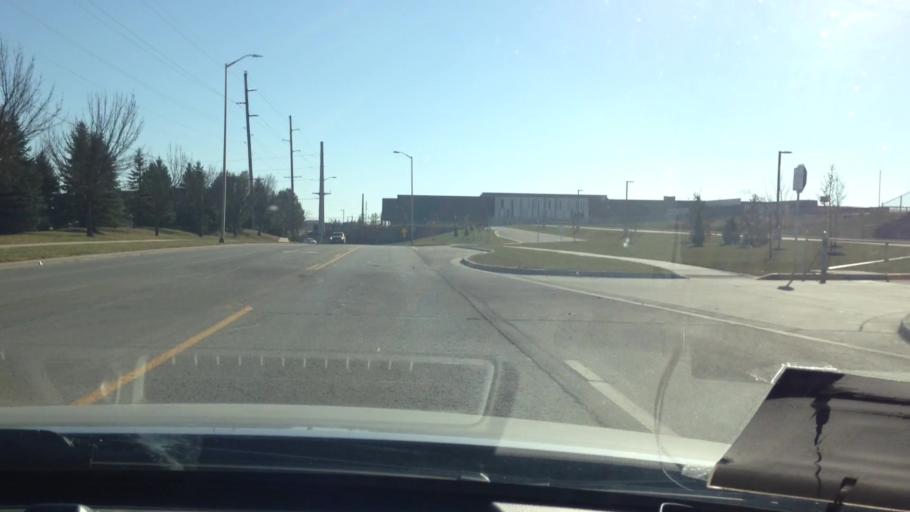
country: US
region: Kansas
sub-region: Johnson County
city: Olathe
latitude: 38.8896
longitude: -94.8527
